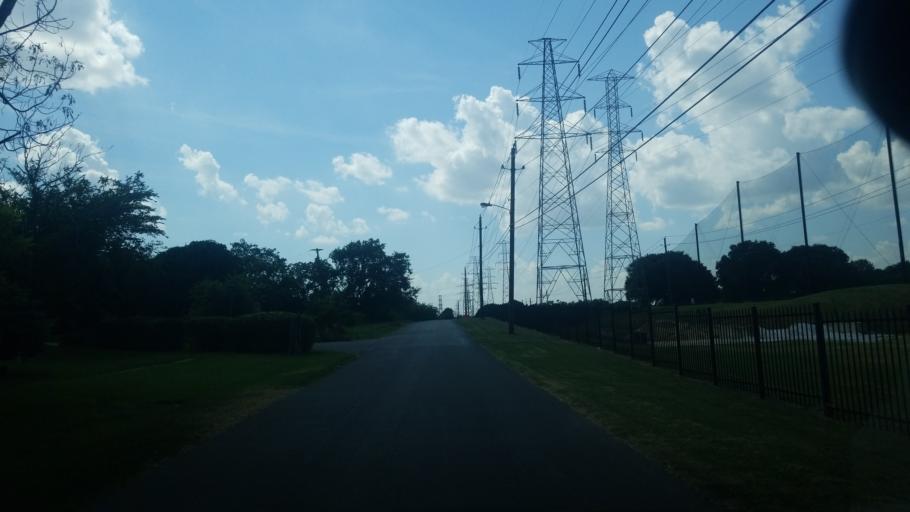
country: US
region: Texas
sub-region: Dallas County
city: Dallas
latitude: 32.7202
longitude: -96.7974
